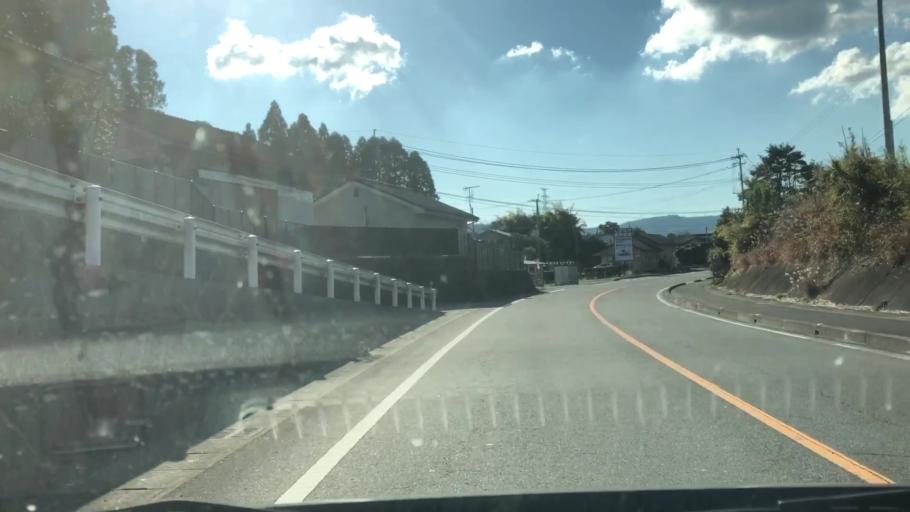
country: JP
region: Kagoshima
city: Satsumasendai
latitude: 31.8575
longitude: 130.3790
